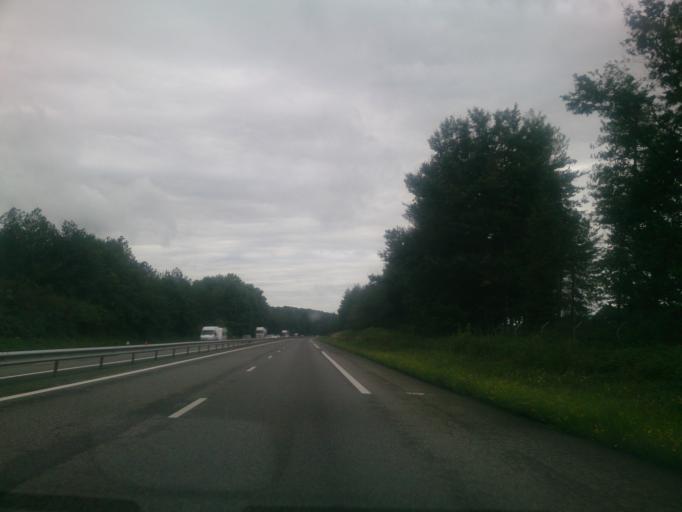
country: FR
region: Midi-Pyrenees
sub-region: Departement de la Haute-Garonne
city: Montrejeau
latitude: 43.0914
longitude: 0.5143
